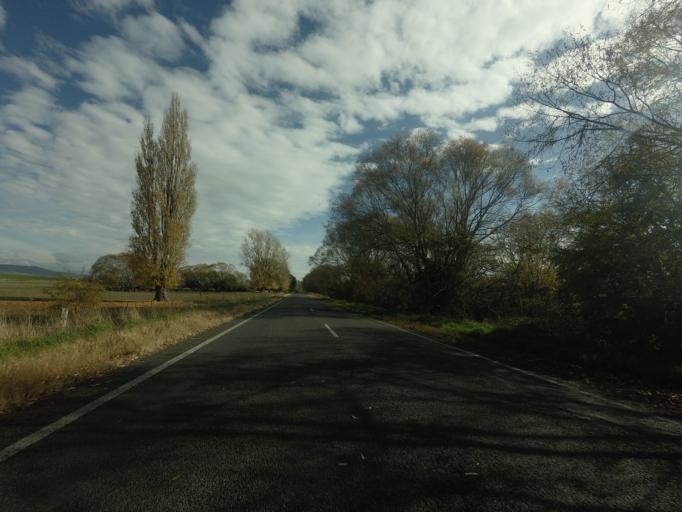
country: AU
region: Tasmania
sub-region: Meander Valley
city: Westbury
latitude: -41.5280
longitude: 146.8036
